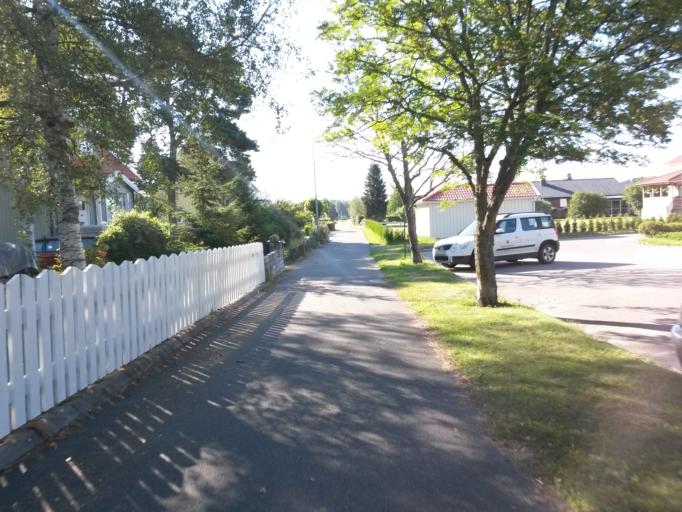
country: SE
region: Vaestra Goetaland
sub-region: Vargarda Kommun
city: Vargarda
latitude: 58.0391
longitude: 12.8120
